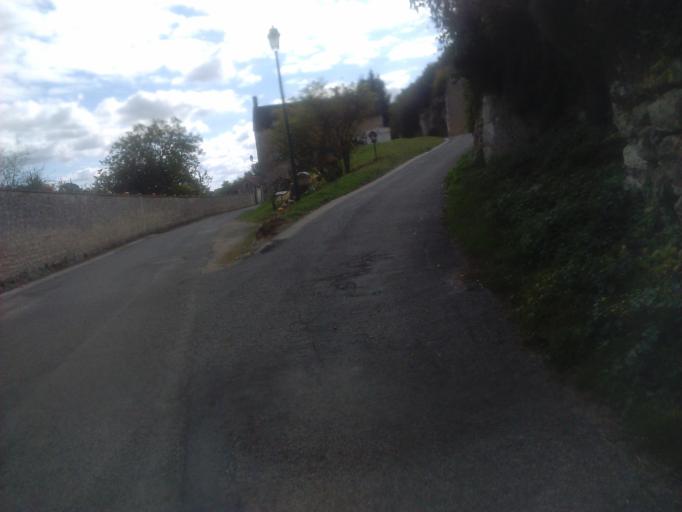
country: FR
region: Centre
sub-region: Departement du Loir-et-Cher
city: Villiers-sur-Loir
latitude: 47.7989
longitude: 0.9808
